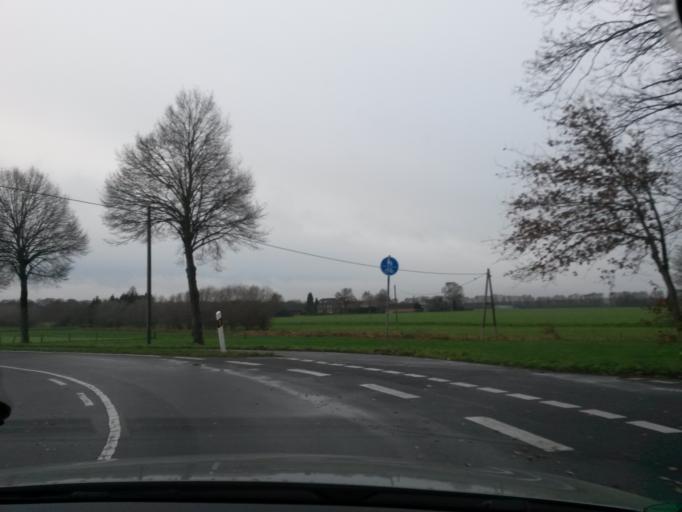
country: DE
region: North Rhine-Westphalia
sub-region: Regierungsbezirk Dusseldorf
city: Alpen
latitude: 51.6012
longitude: 6.5016
